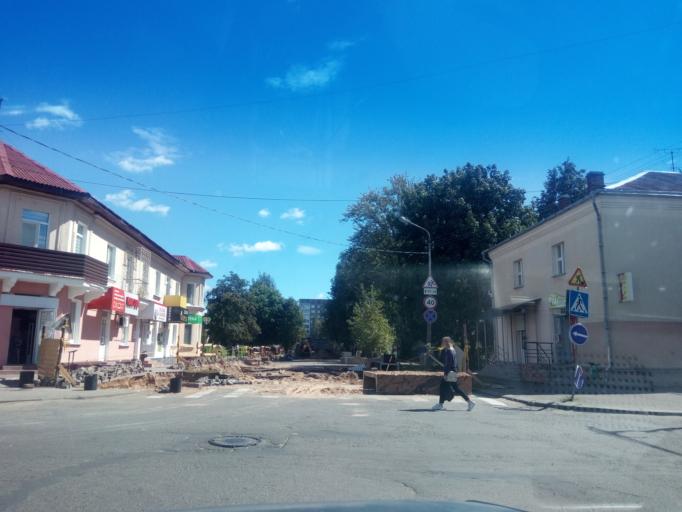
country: BY
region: Vitebsk
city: Polatsk
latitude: 55.4876
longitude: 28.7833
